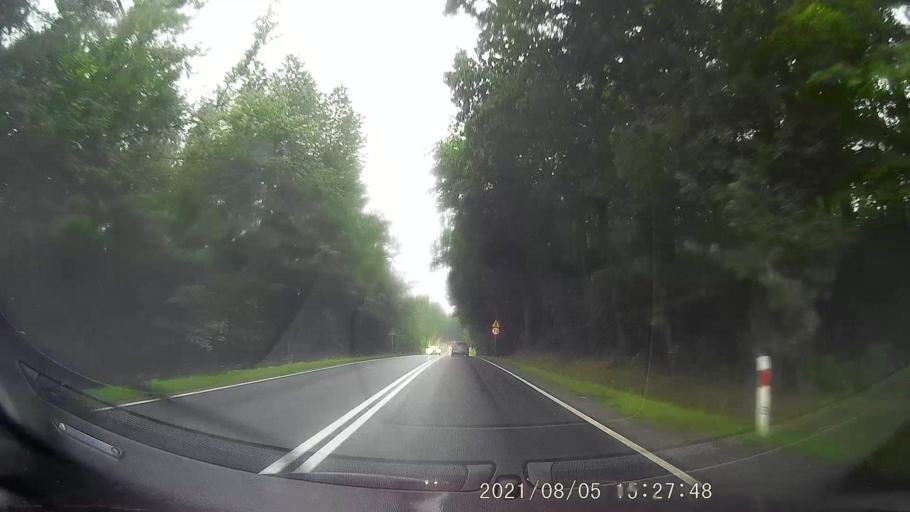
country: PL
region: Lower Silesian Voivodeship
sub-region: Powiat klodzki
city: Klodzko
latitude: 50.4297
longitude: 16.7240
